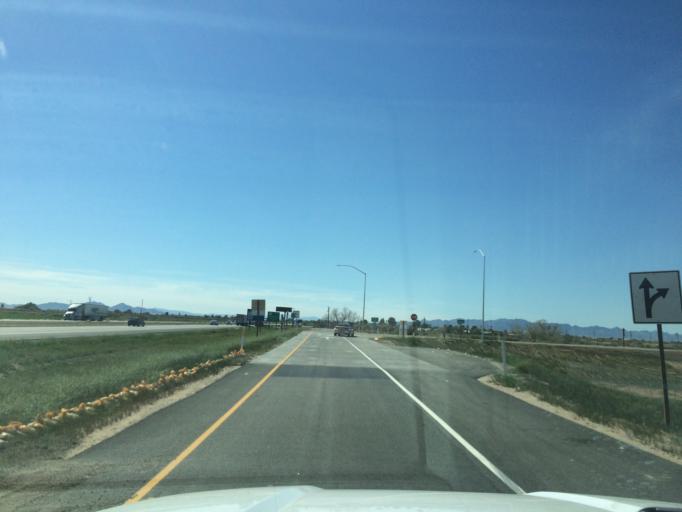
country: US
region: Arizona
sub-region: La Paz County
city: Ehrenberg
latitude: 33.6082
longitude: -114.5473
